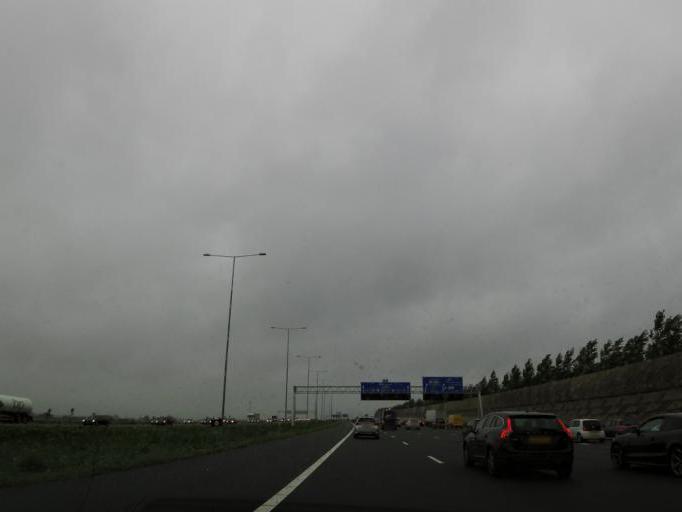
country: NL
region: North Holland
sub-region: Gemeente Amsterdam
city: Amsterdam-Zuidoost
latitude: 52.2733
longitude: 4.9580
